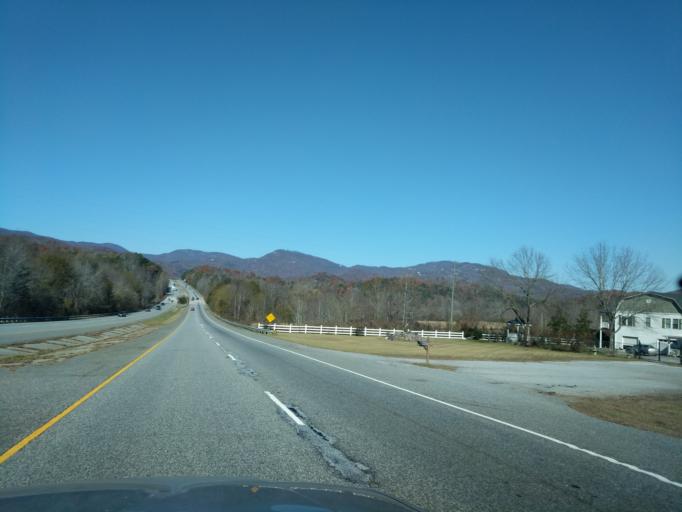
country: US
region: South Carolina
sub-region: Greenville County
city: Slater-Marietta
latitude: 35.1072
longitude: -82.4540
